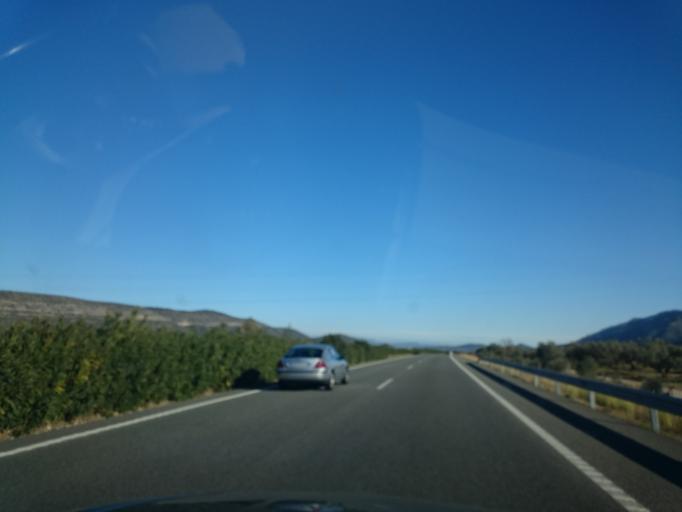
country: ES
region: Catalonia
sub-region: Provincia de Tarragona
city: Ulldecona
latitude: 40.6143
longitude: 0.4796
